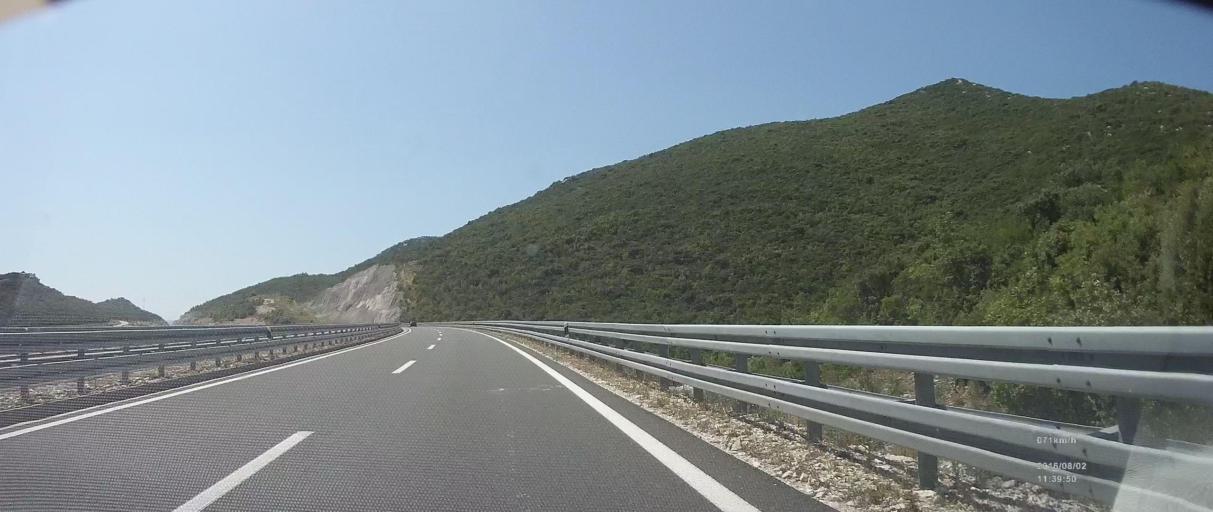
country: HR
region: Dubrovacko-Neretvanska
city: Komin
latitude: 43.0819
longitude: 17.4900
